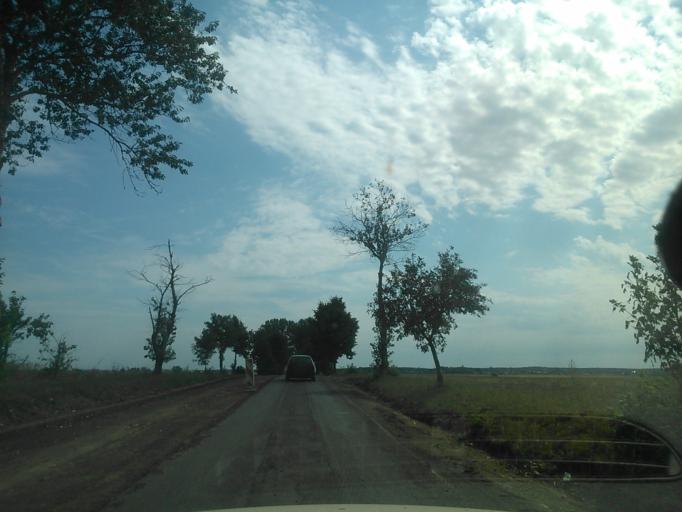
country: PL
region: Warmian-Masurian Voivodeship
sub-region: Powiat dzialdowski
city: Ilowo -Osada
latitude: 53.1900
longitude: 20.2774
